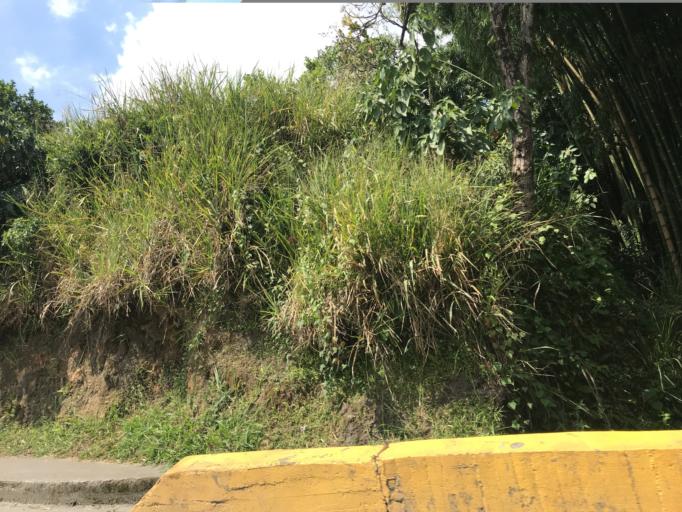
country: CO
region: Quindio
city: Calarca
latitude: 4.5244
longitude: -75.6378
